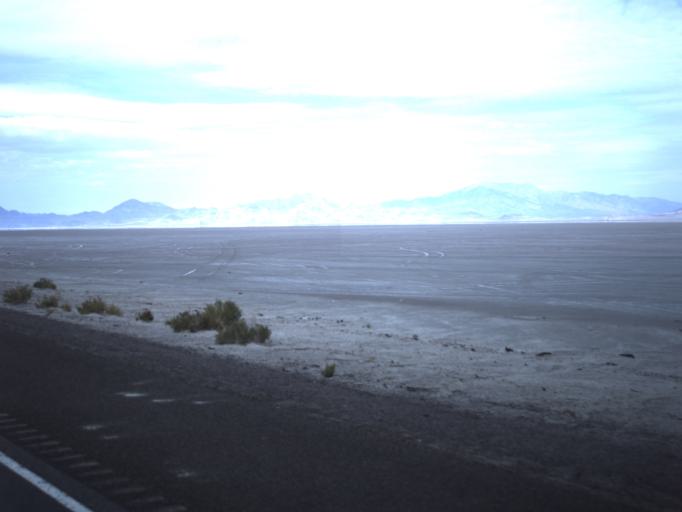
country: US
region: Utah
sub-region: Tooele County
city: Wendover
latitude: 40.7371
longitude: -113.7382
